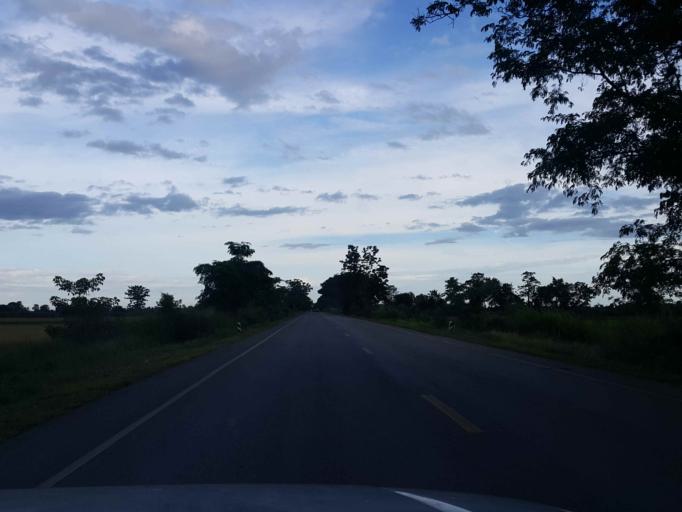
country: TH
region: Sukhothai
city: Sawankhalok
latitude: 17.3879
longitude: 99.7342
